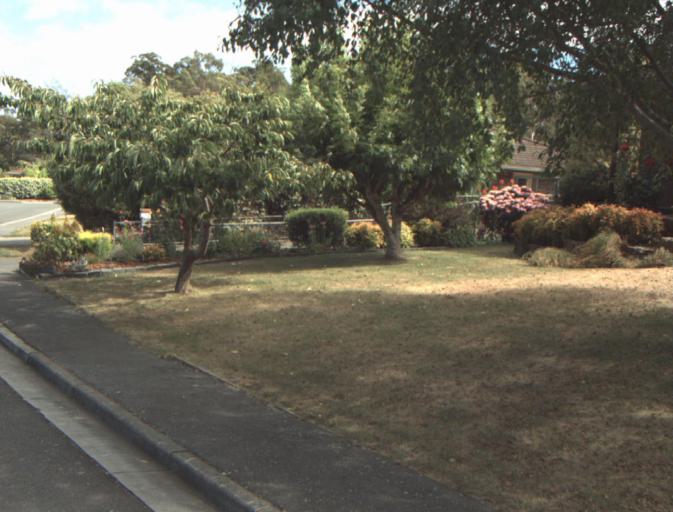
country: AU
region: Tasmania
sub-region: Launceston
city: West Launceston
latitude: -41.4576
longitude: 147.1281
